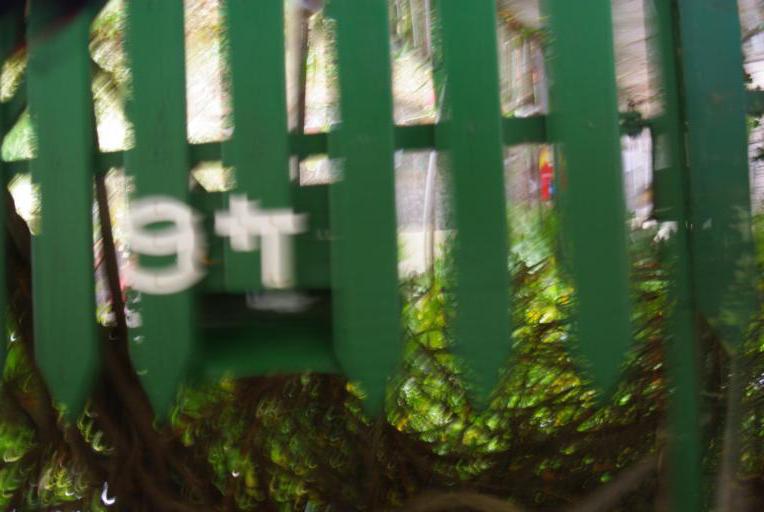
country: HU
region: Pest
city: Pecel
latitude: 47.4915
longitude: 19.3503
